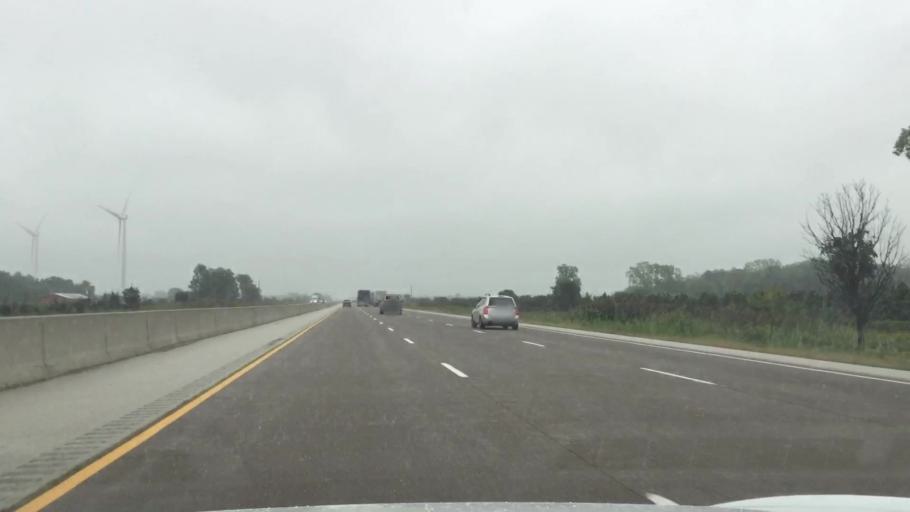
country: US
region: Michigan
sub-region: Wayne County
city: Grosse Pointe
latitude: 42.2374
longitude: -82.7428
